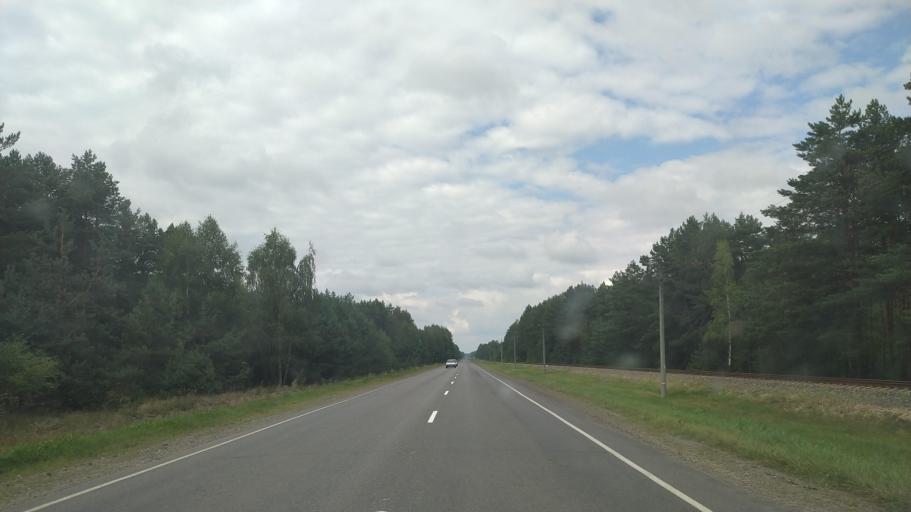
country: BY
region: Brest
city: Byelaazyorsk
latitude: 52.5243
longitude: 25.1483
